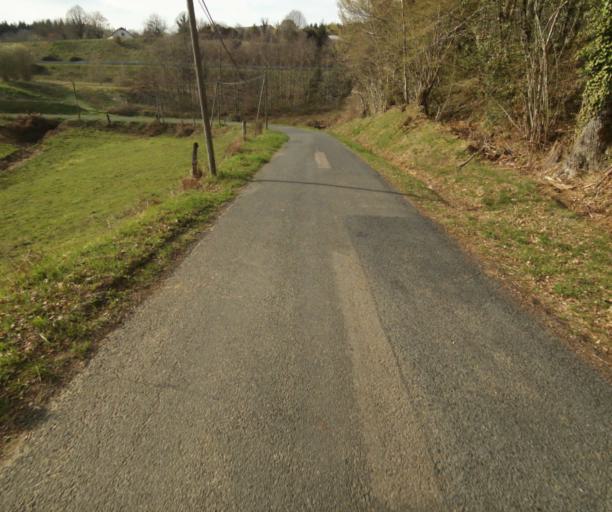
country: FR
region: Limousin
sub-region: Departement de la Correze
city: Naves
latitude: 45.3166
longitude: 1.7430
